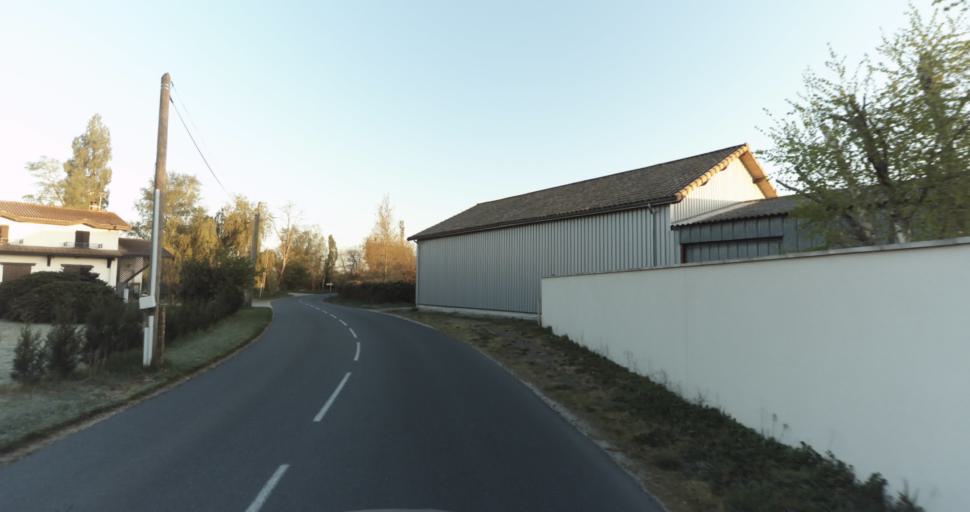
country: FR
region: Aquitaine
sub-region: Departement de la Gironde
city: Martignas-sur-Jalle
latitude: 44.8152
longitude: -0.7485
